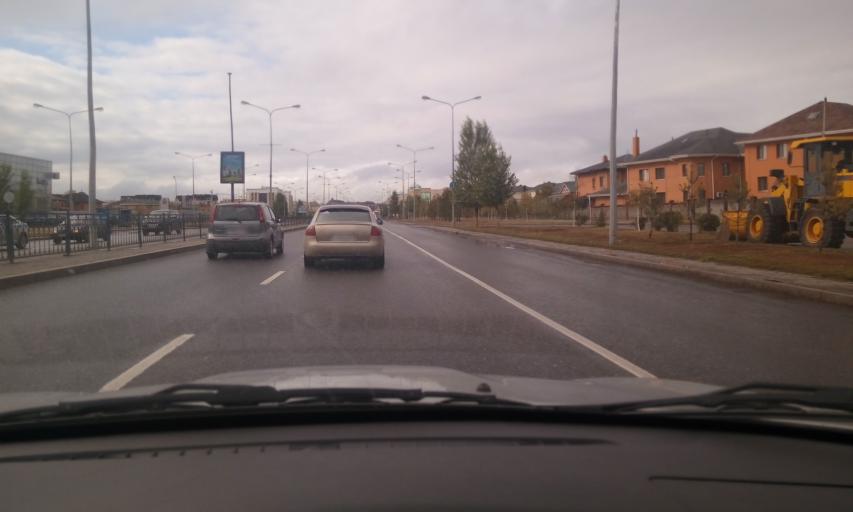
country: KZ
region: Astana Qalasy
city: Astana
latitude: 51.1467
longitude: 71.4019
